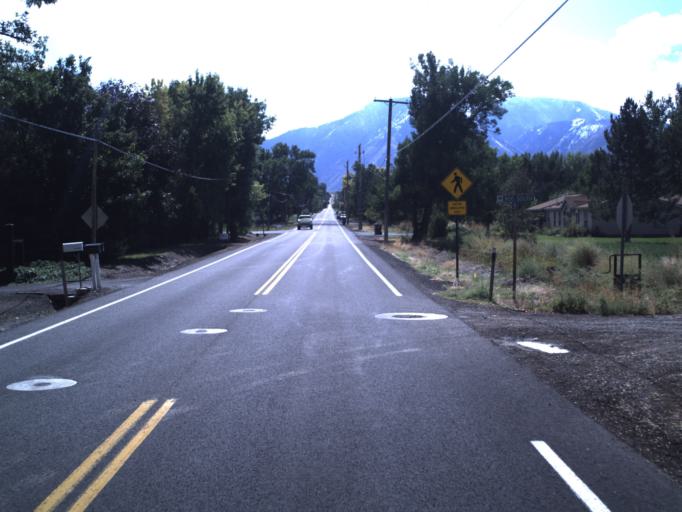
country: US
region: Utah
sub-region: Utah County
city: Mapleton
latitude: 40.1233
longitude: -111.5788
